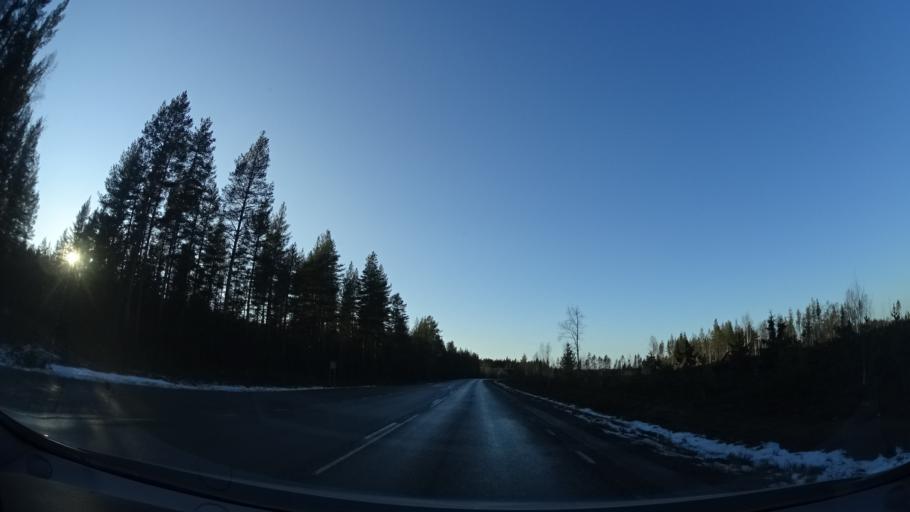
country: SE
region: Vaesterbotten
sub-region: Norsjo Kommun
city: Norsjoe
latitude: 64.9803
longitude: 19.5794
